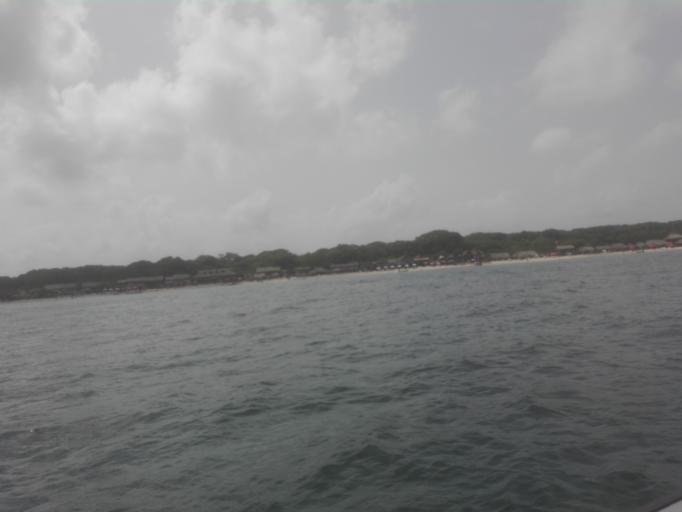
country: CO
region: Bolivar
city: Turbana
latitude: 10.2254
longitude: -75.6102
